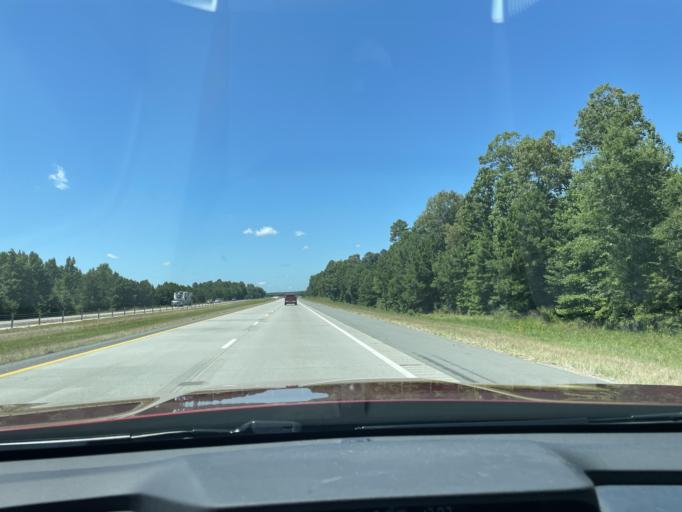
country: US
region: Arkansas
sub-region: Jefferson County
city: Pine Bluff
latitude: 34.1858
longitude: -91.9828
